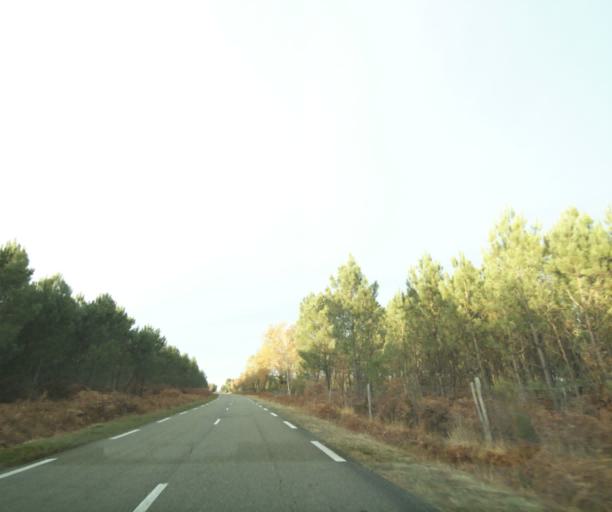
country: FR
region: Aquitaine
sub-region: Departement des Landes
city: Gabarret
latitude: 44.1207
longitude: -0.1071
